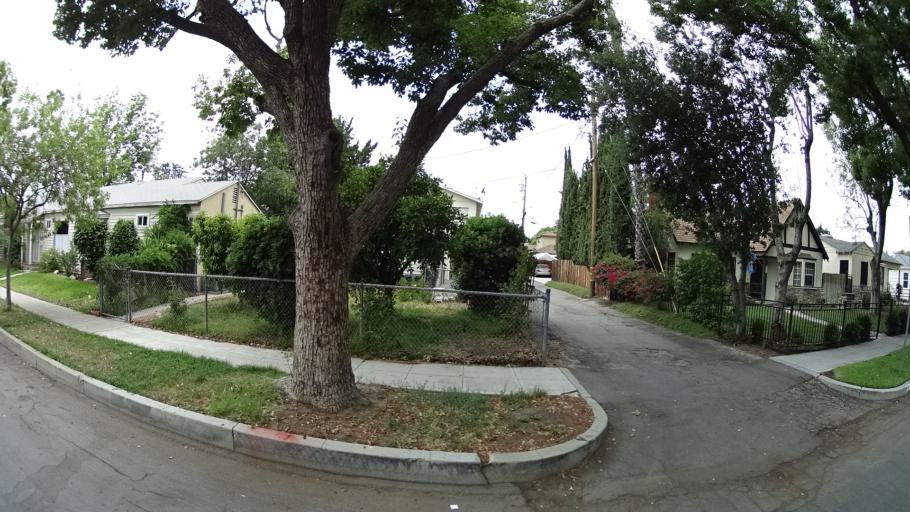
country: US
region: California
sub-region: Los Angeles County
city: Burbank
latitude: 34.1687
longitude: -118.3343
